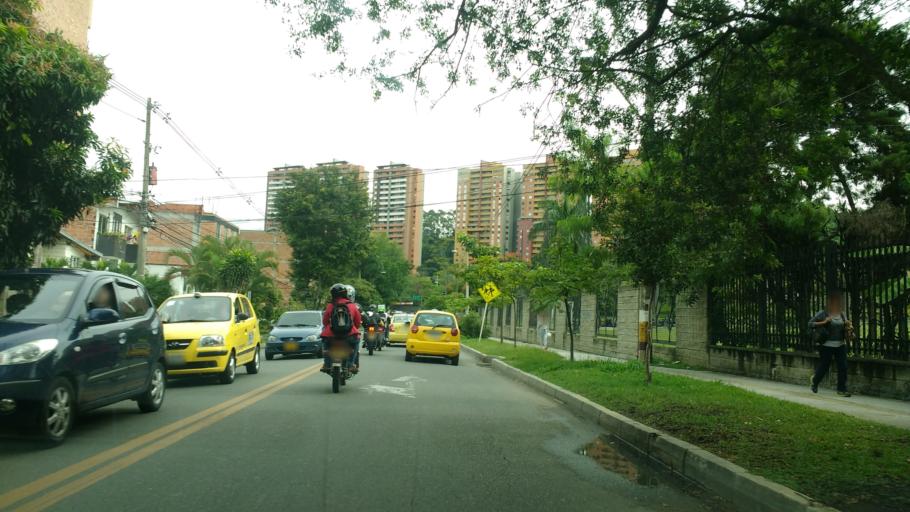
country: CO
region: Antioquia
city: Medellin
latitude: 6.2410
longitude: -75.6080
